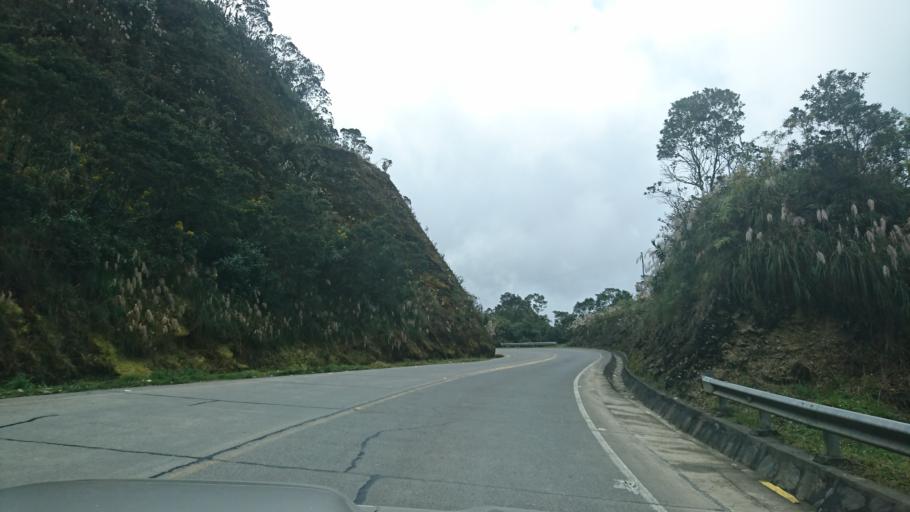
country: BO
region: La Paz
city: Coroico
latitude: -16.2855
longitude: -67.8447
